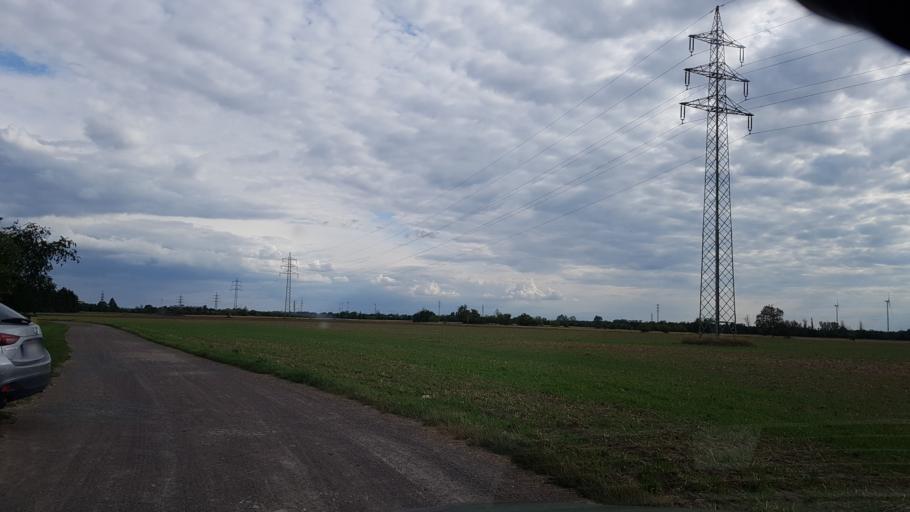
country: DE
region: Brandenburg
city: Falkenberg
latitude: 51.5804
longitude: 13.2257
